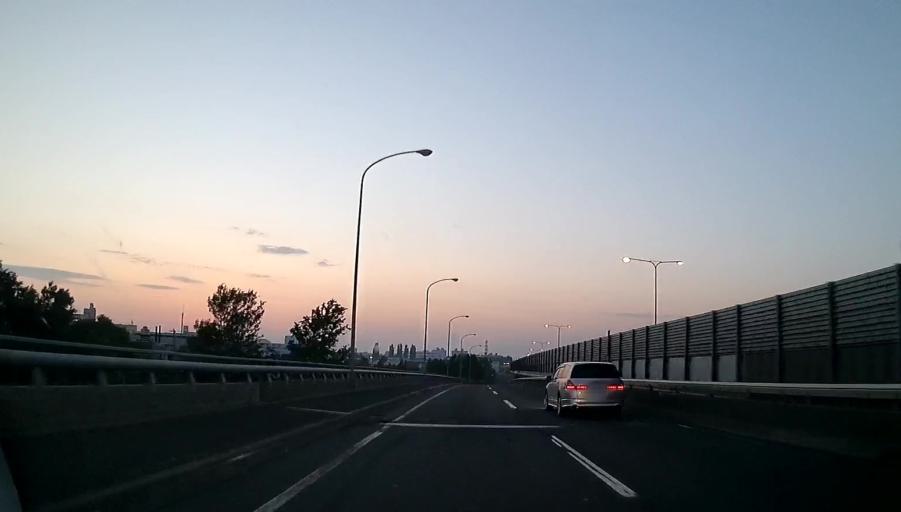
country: JP
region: Hokkaido
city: Sapporo
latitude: 43.0292
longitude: 141.4468
